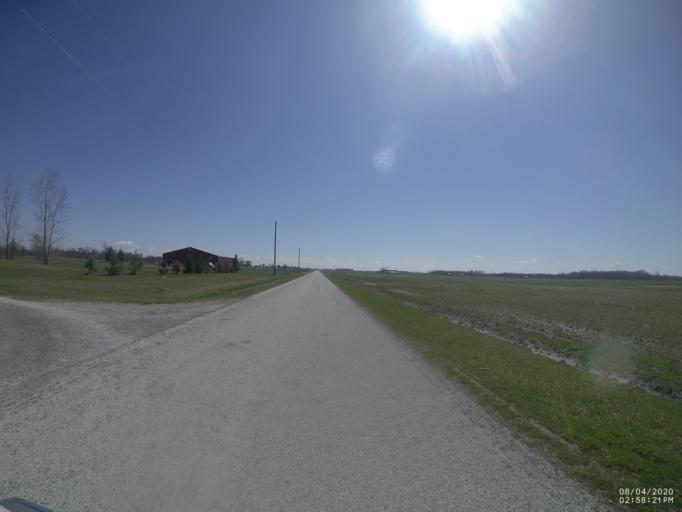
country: US
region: Ohio
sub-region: Sandusky County
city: Gibsonburg
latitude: 41.3260
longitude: -83.2542
